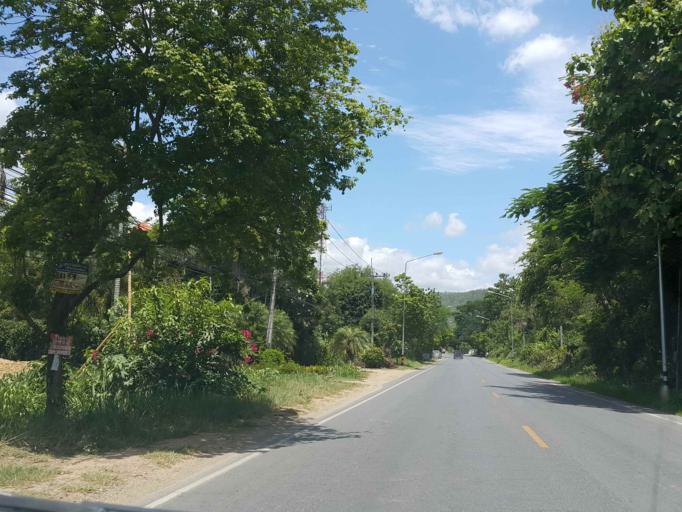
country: TH
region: Chiang Mai
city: Hang Dong
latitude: 18.7265
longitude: 98.9150
